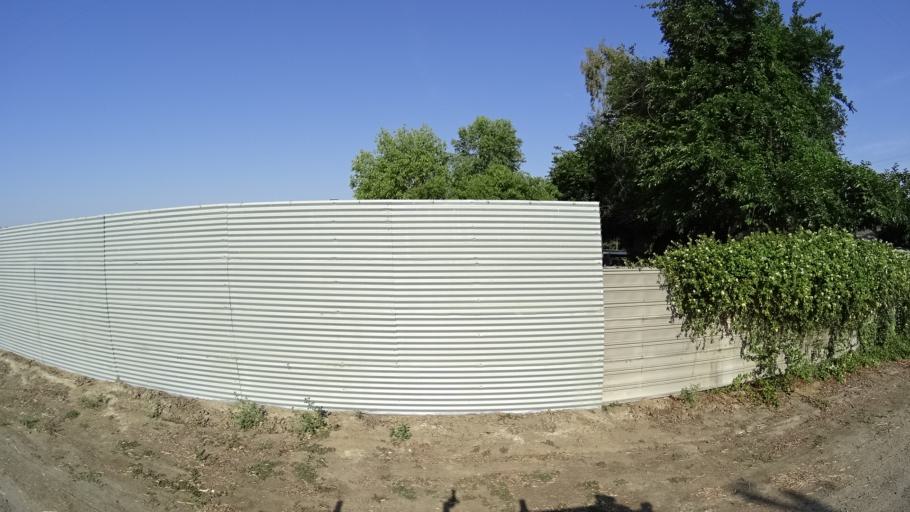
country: US
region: California
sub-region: Kings County
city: Lemoore
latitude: 36.3654
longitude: -119.8161
